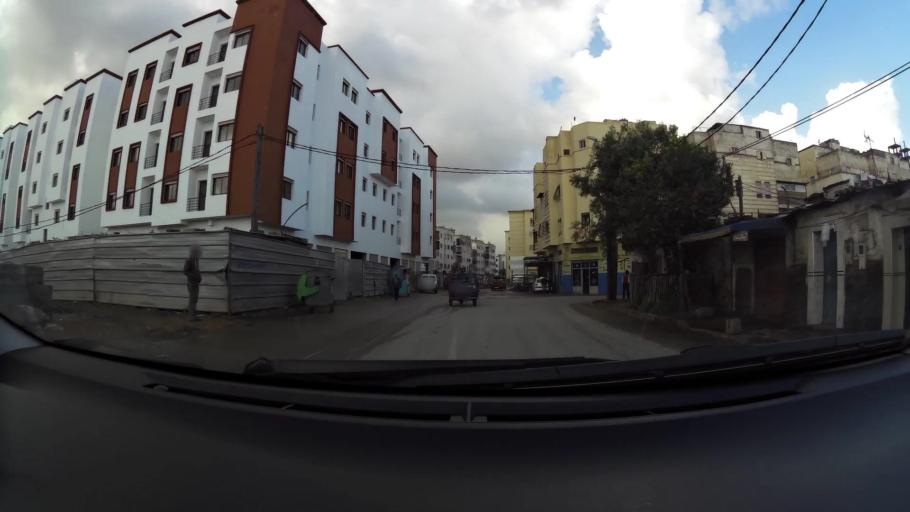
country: MA
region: Grand Casablanca
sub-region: Mediouna
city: Tit Mellil
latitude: 33.5812
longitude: -7.5348
